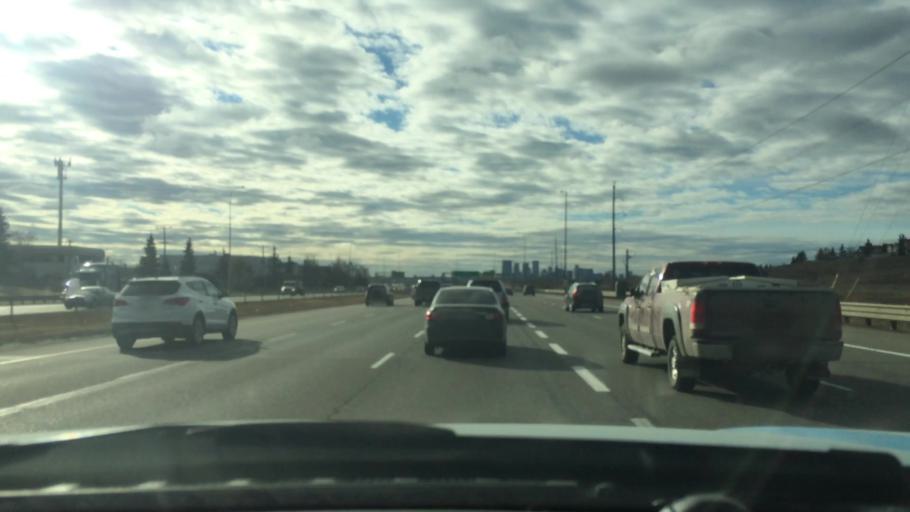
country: CA
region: Alberta
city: Calgary
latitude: 51.1191
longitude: -114.0467
